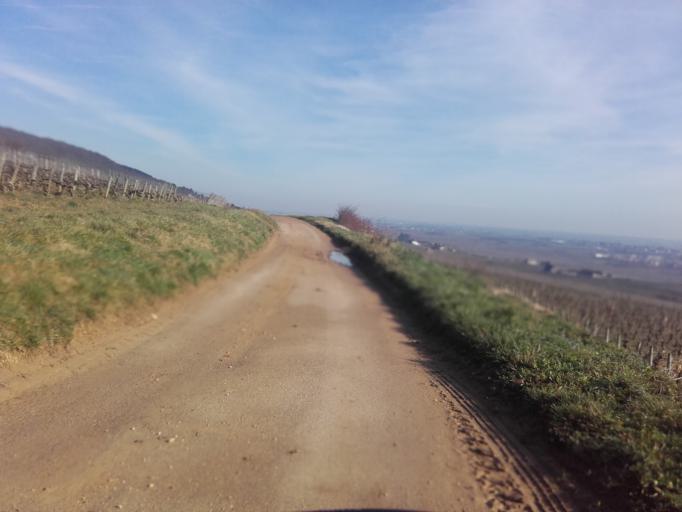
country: FR
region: Bourgogne
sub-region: Departement de la Cote-d'Or
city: Corpeau
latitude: 46.9207
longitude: 4.7084
